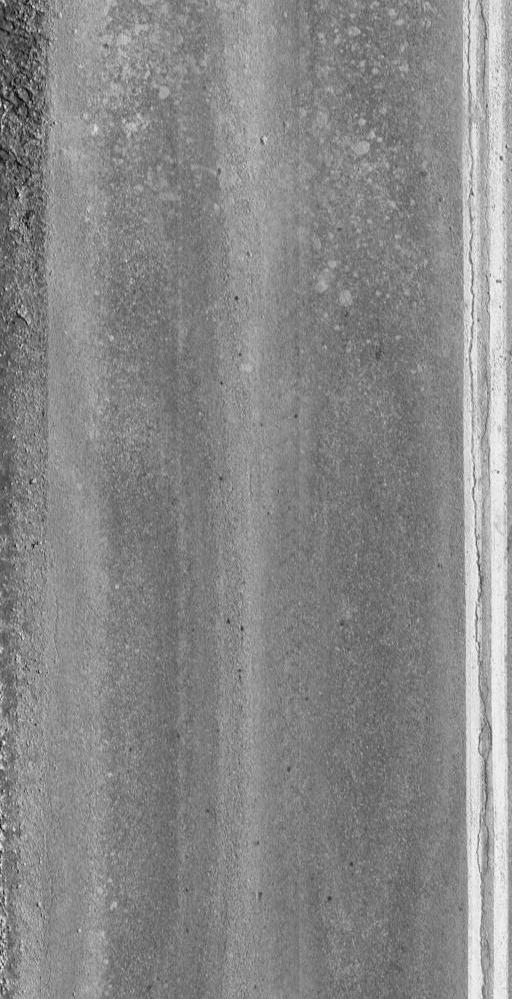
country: US
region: Vermont
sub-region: Chittenden County
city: South Burlington
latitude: 44.4004
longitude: -73.1771
